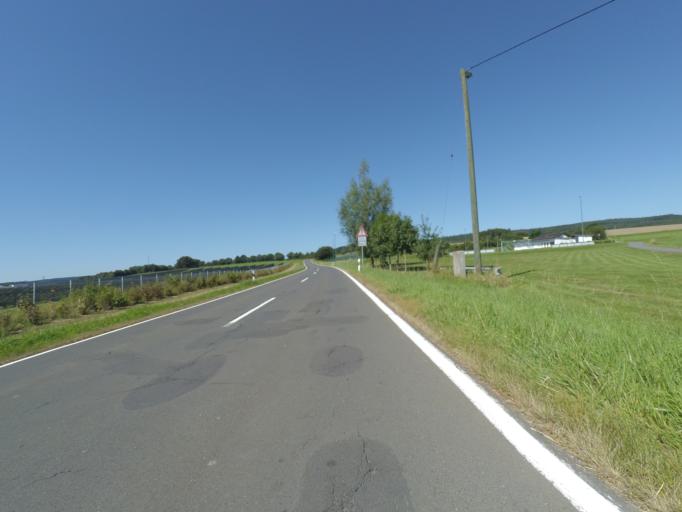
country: DE
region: Rheinland-Pfalz
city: Grosslittgen
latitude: 50.0294
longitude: 6.7936
